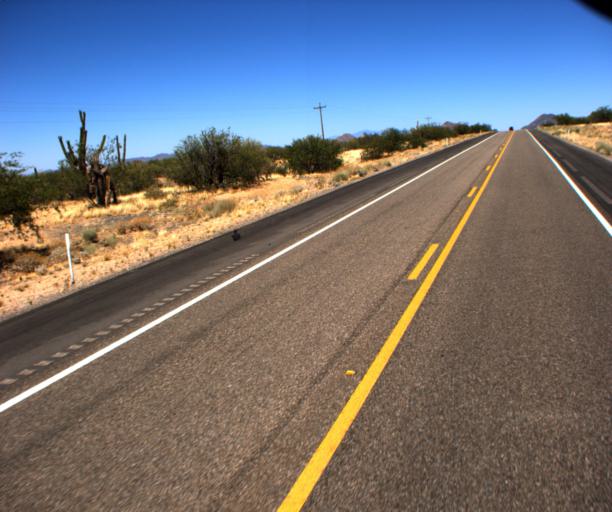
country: US
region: Arizona
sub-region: Pima County
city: Three Points
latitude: 32.0301
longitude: -111.5626
